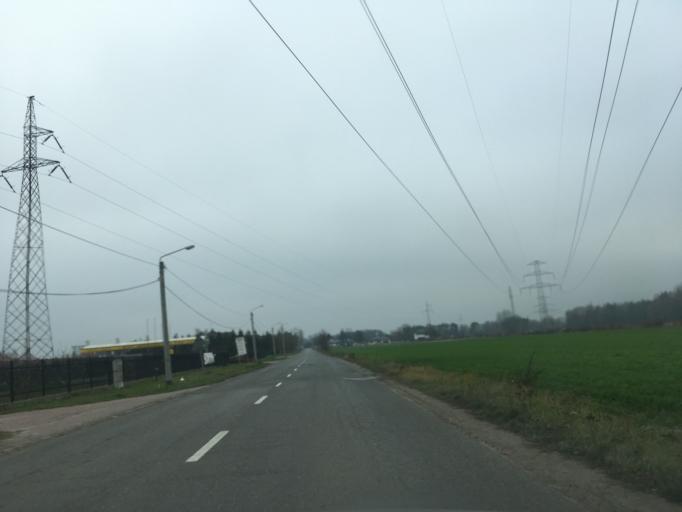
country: PL
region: Masovian Voivodeship
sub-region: Powiat piaseczynski
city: Lesznowola
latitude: 52.0802
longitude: 20.9674
